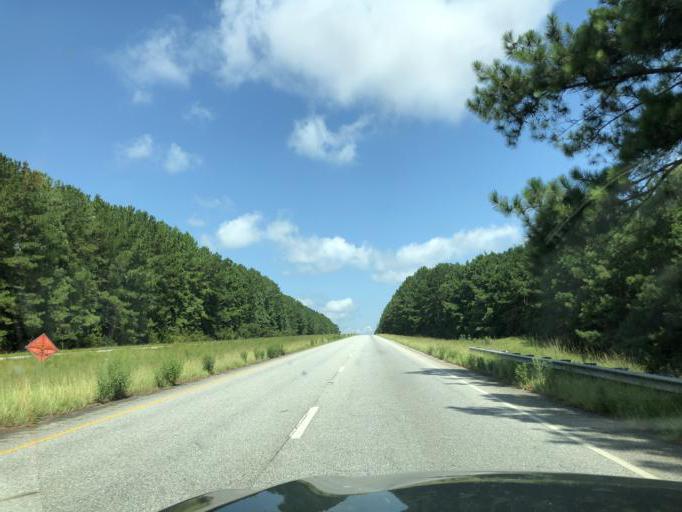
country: US
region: Alabama
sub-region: Henry County
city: Abbeville
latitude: 31.6817
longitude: -85.2791
